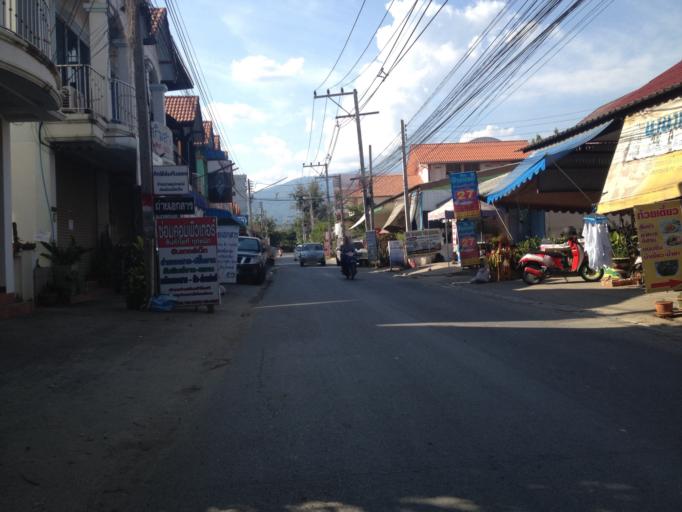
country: TH
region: Chiang Mai
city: Chiang Mai
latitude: 18.7632
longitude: 98.9784
